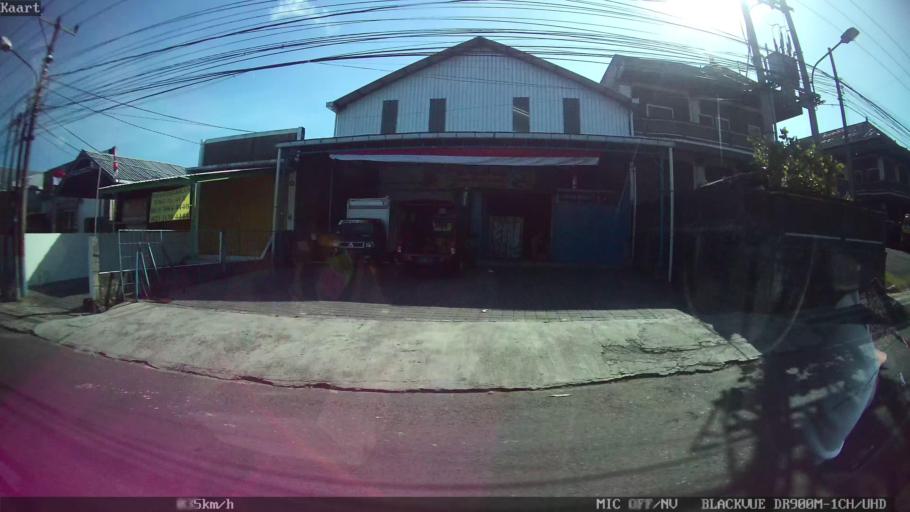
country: ID
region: Bali
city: Banjar Kertasari
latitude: -8.6194
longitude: 115.1904
